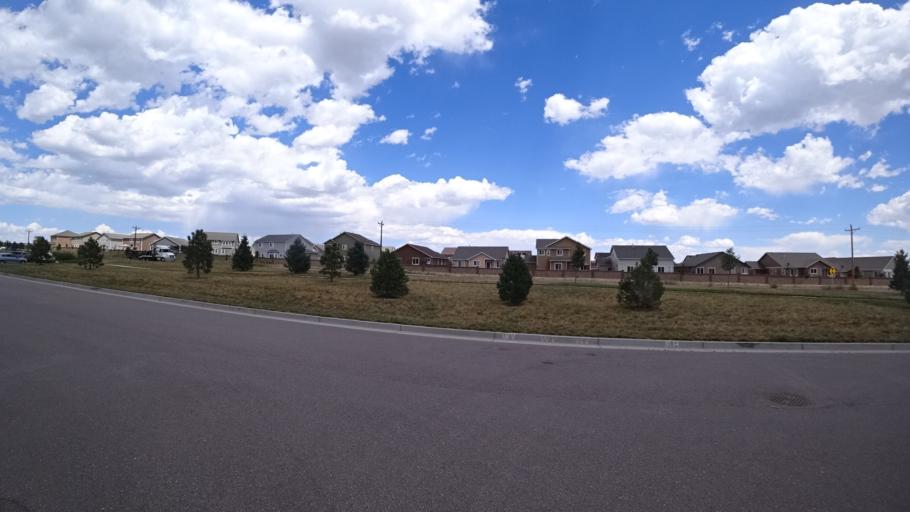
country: US
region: Colorado
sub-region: El Paso County
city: Black Forest
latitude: 38.9527
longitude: -104.7013
